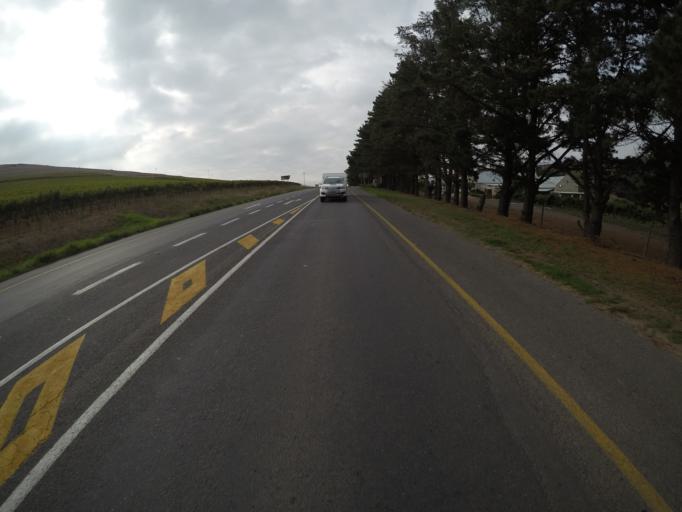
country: ZA
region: Western Cape
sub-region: City of Cape Town
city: Sunset Beach
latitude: -33.8363
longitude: 18.5915
